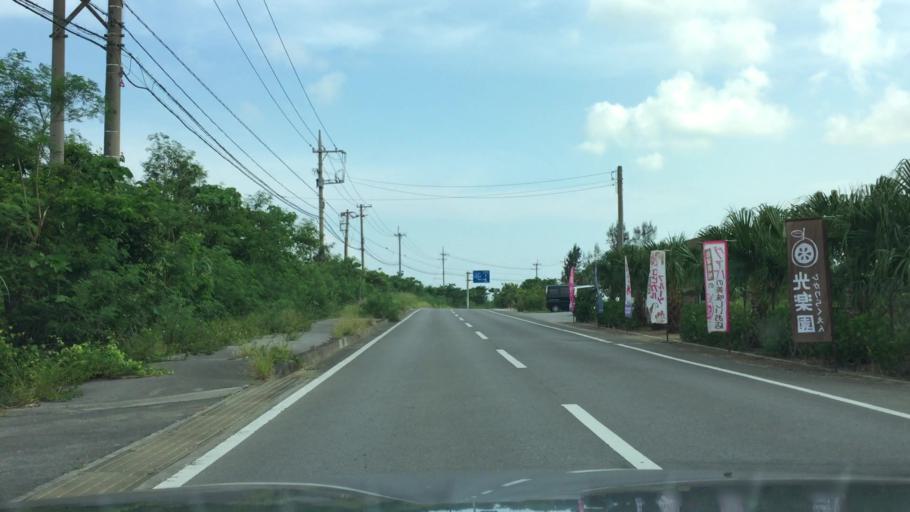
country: JP
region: Okinawa
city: Ishigaki
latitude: 24.3959
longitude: 124.1953
